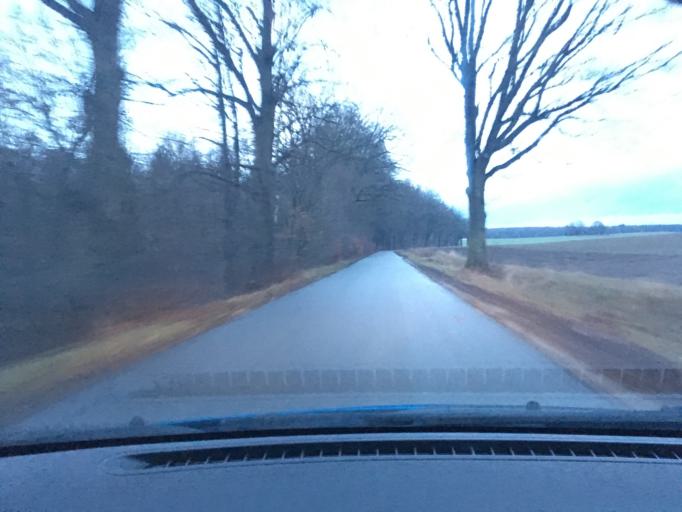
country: DE
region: Lower Saxony
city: Betzendorf
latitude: 53.1485
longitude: 10.3337
